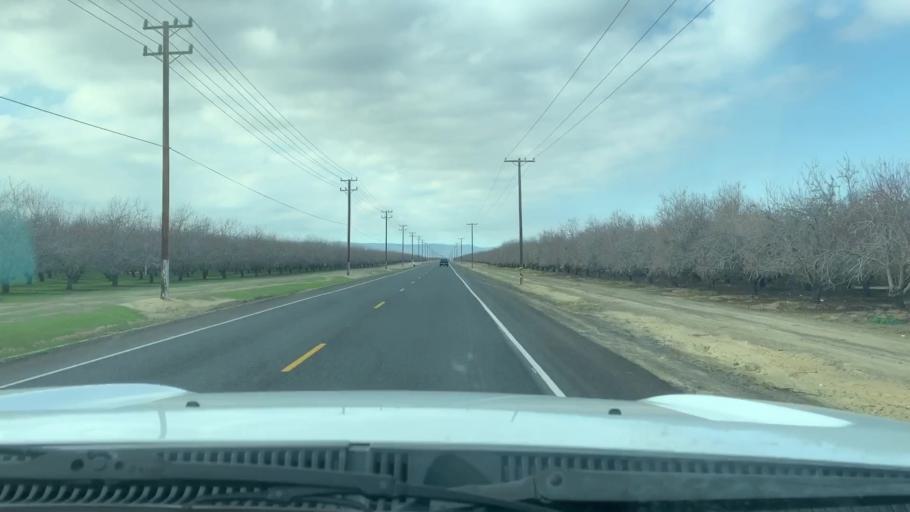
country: US
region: California
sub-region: Kern County
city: Lost Hills
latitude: 35.4993
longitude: -119.6777
